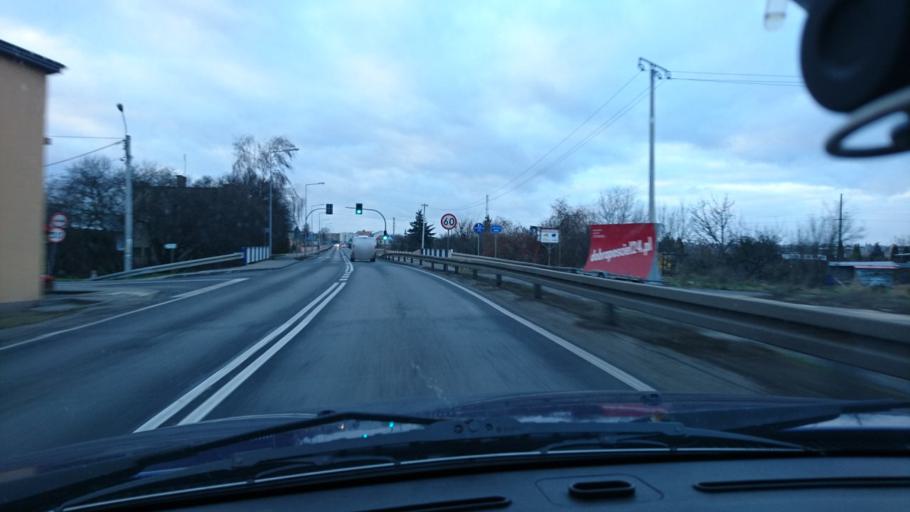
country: PL
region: Greater Poland Voivodeship
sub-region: Powiat kepinski
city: Baranow
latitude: 51.2687
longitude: 17.9978
